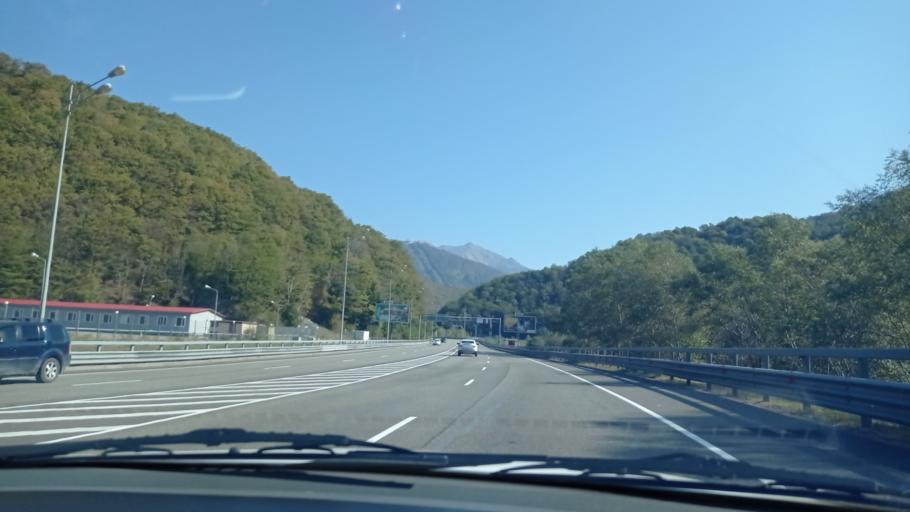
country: RU
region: Krasnodarskiy
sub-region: Sochi City
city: Krasnaya Polyana
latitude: 43.6851
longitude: 40.2381
